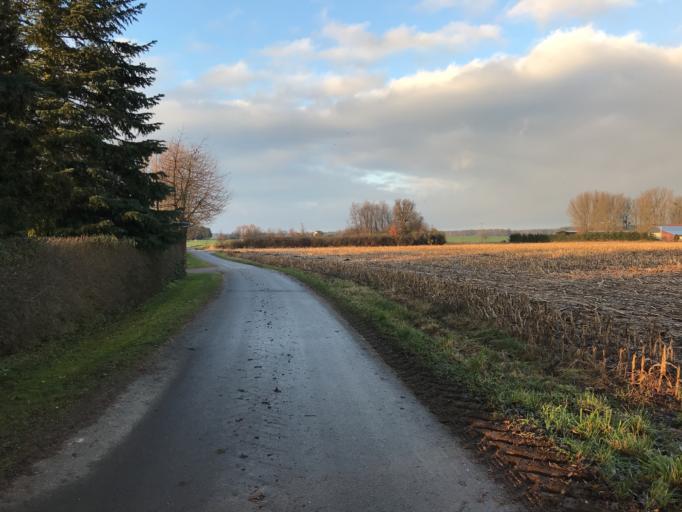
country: DE
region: Mecklenburg-Vorpommern
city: Blankensee
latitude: 53.4095
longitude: 13.2402
